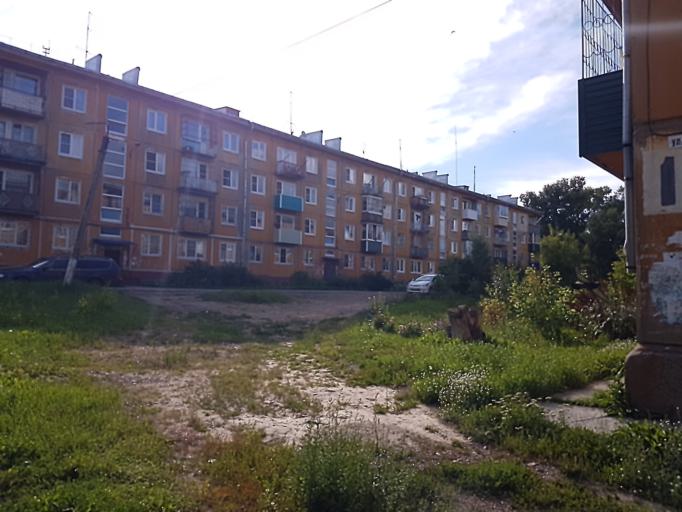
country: RU
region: Irkutsk
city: Usol'ye-Sibirskoye
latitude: 52.7572
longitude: 103.6338
